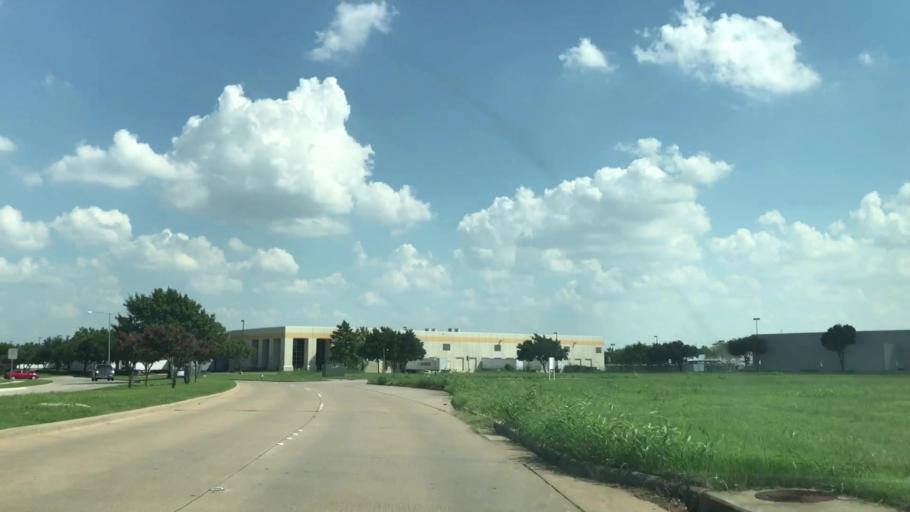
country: US
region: Texas
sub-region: Denton County
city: Lewisville
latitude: 33.0154
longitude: -96.9772
